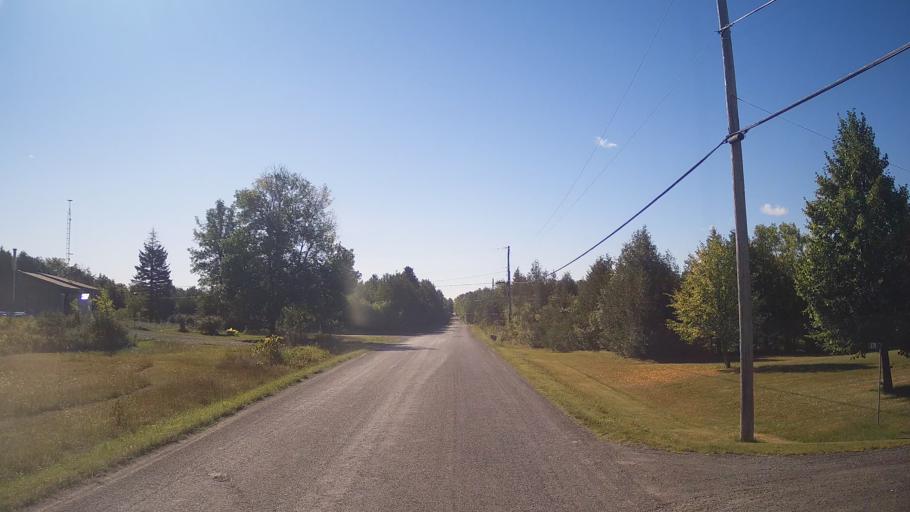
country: CA
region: Ontario
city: Prescott
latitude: 44.9897
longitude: -75.5870
